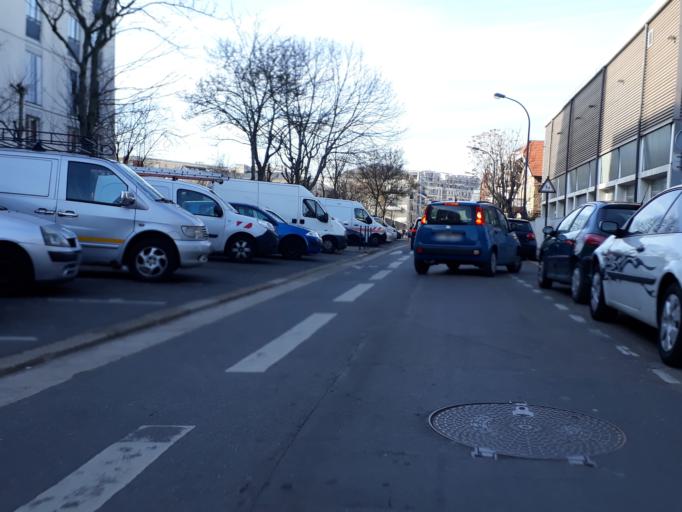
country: FR
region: Ile-de-France
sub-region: Departement des Hauts-de-Seine
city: Bois-Colombes
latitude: 48.9248
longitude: 2.2773
